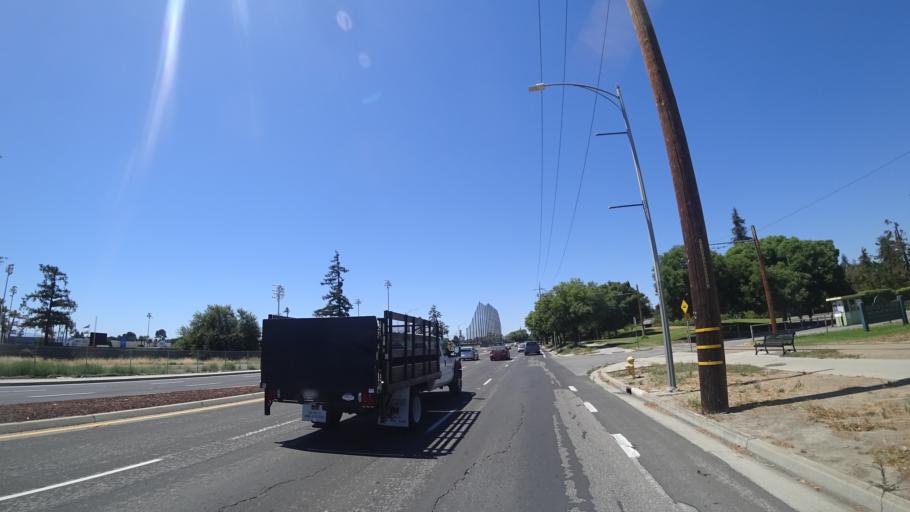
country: US
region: California
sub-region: Santa Clara County
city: San Jose
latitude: 37.3202
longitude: -121.8603
